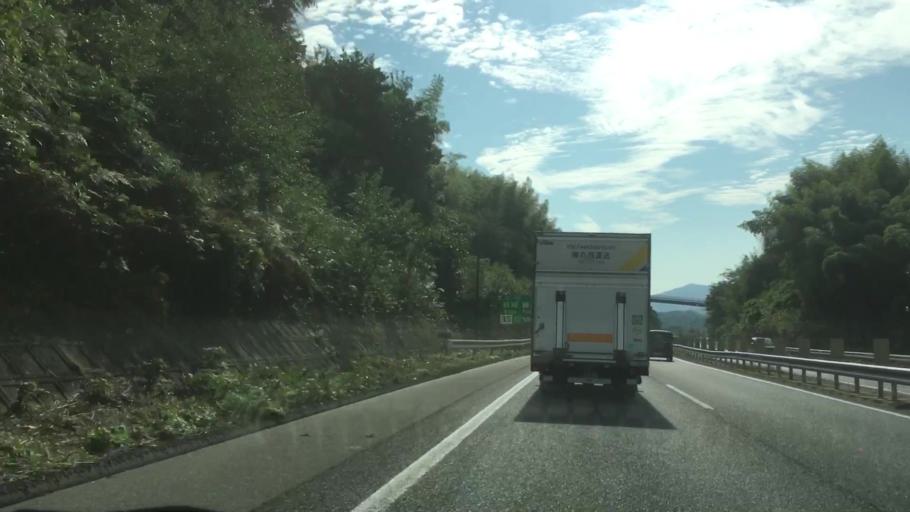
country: JP
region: Yamaguchi
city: Yanai
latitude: 34.0859
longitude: 132.0894
